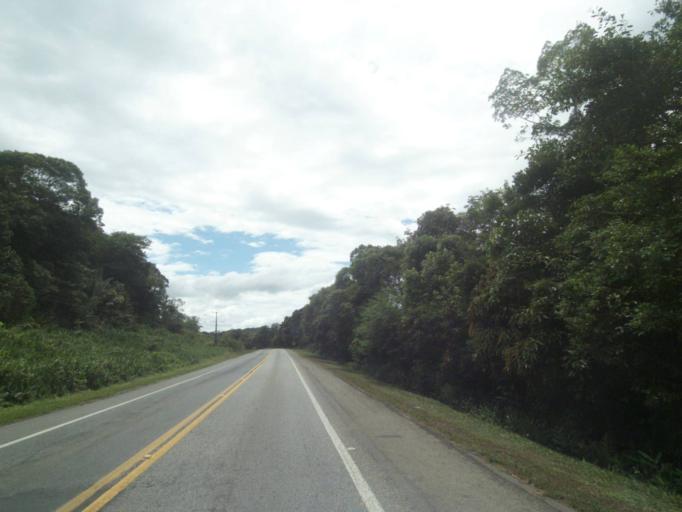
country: BR
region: Parana
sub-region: Antonina
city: Antonina
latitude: -25.4488
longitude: -48.7745
